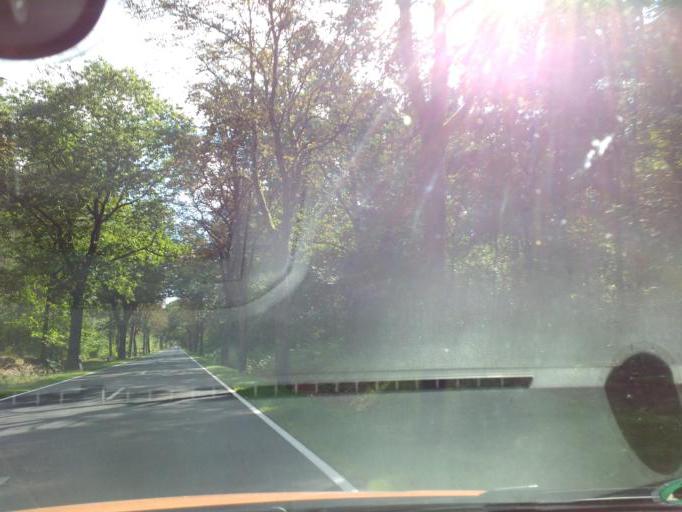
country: DE
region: Brandenburg
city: Birkenwerder
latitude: 52.7340
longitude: 13.2929
